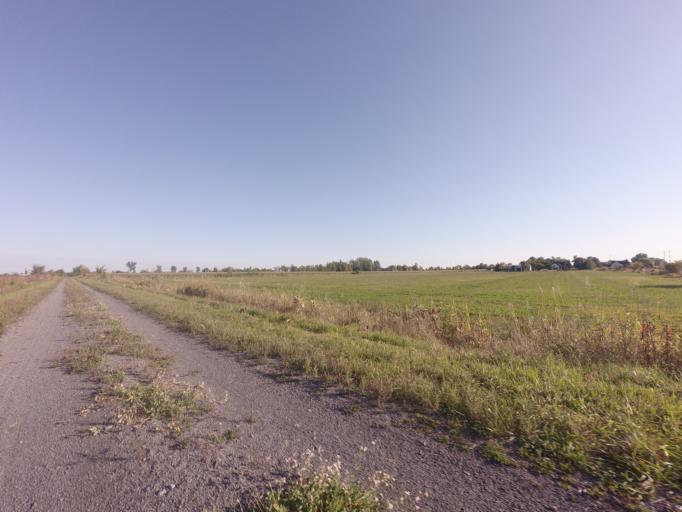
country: CA
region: Ontario
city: Hawkesbury
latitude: 45.5146
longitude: -74.5127
